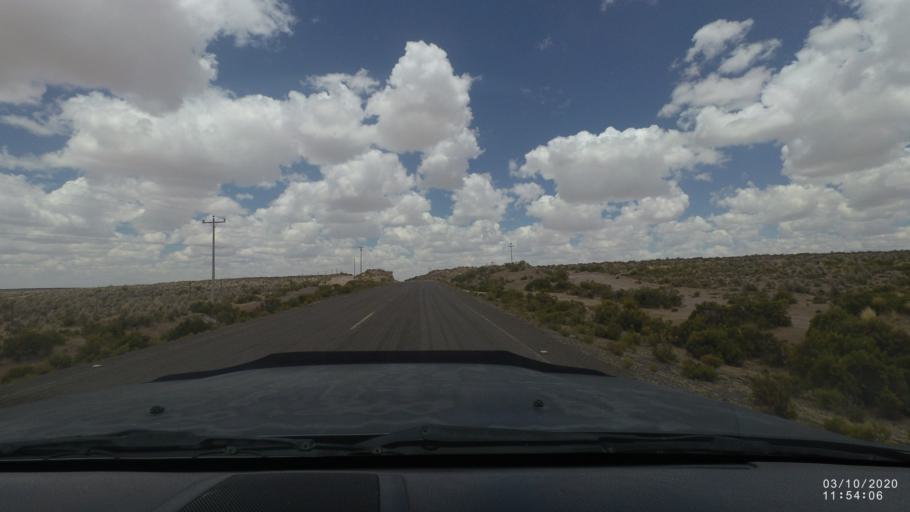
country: BO
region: Oruro
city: Poopo
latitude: -18.4894
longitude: -67.6069
